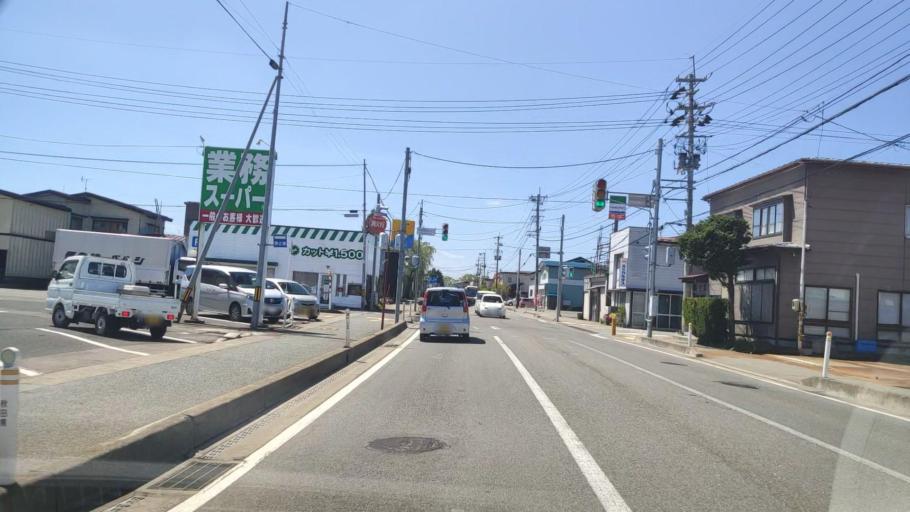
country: JP
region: Akita
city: Omagari
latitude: 39.4534
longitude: 140.4733
